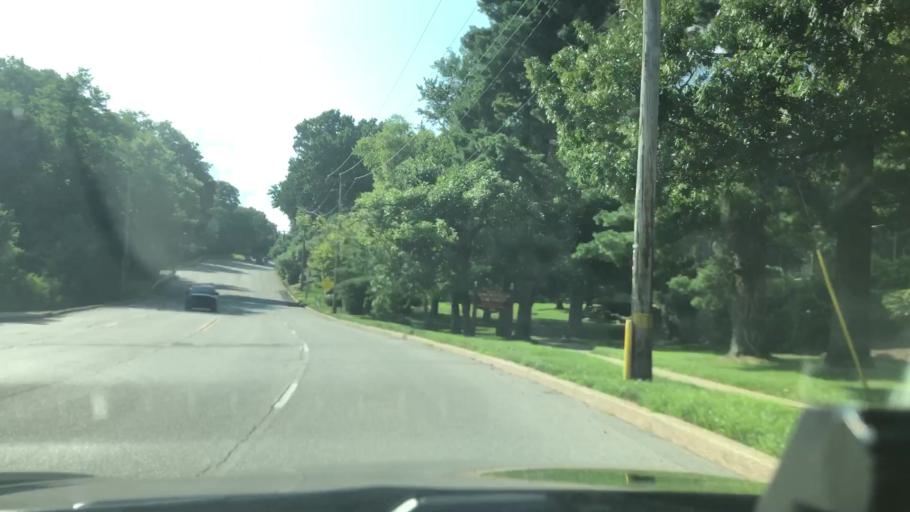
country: US
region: Pennsylvania
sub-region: Montgomery County
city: Wyndmoor
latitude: 40.0925
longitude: -75.1882
